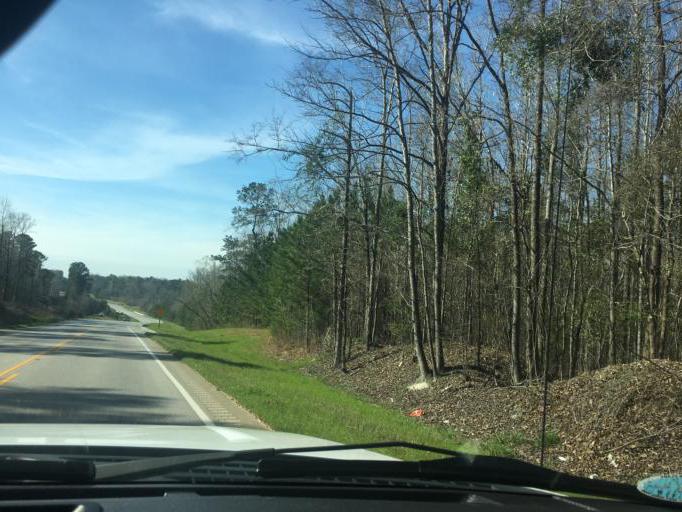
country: US
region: Alabama
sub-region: Lee County
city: Auburn
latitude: 32.4299
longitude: -85.4629
